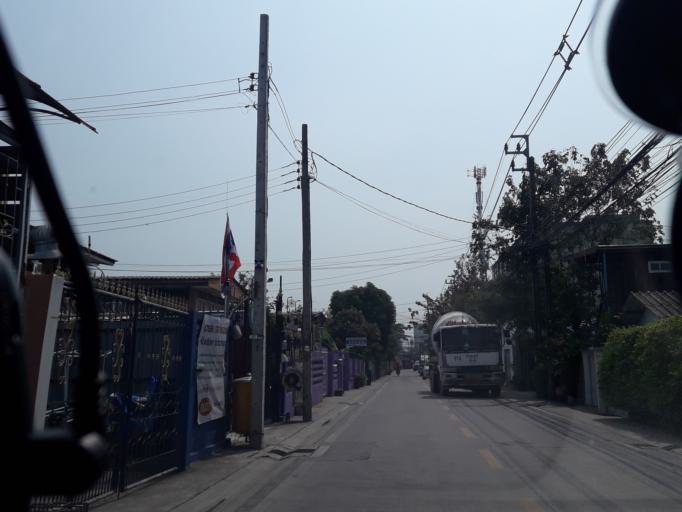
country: TH
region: Bangkok
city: Min Buri
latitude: 13.8148
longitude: 100.7056
